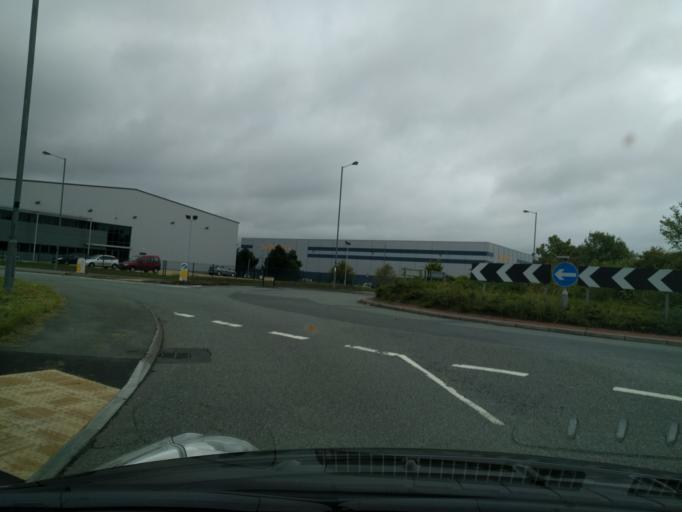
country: GB
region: England
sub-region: Borough of Wigan
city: Ashton in Makerfield
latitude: 53.4748
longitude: -2.6568
